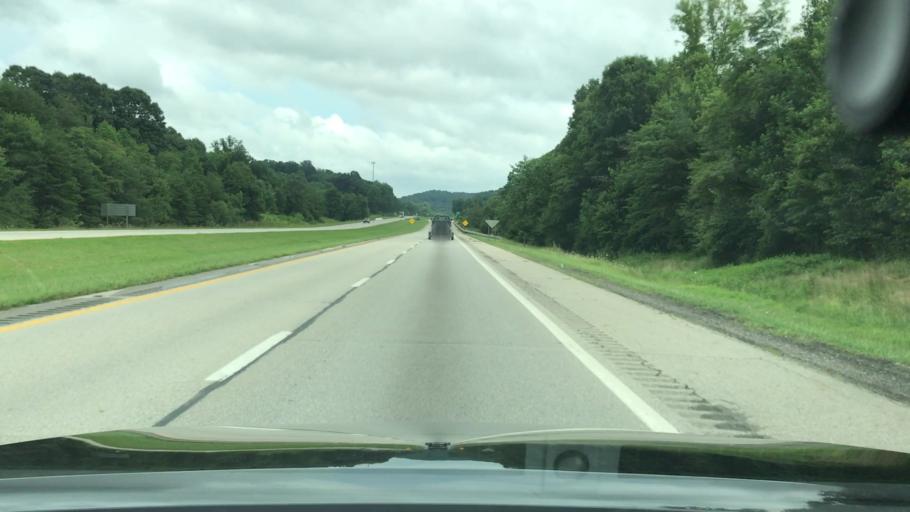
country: US
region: Ohio
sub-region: Jackson County
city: Jackson
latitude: 39.0853
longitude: -82.6428
